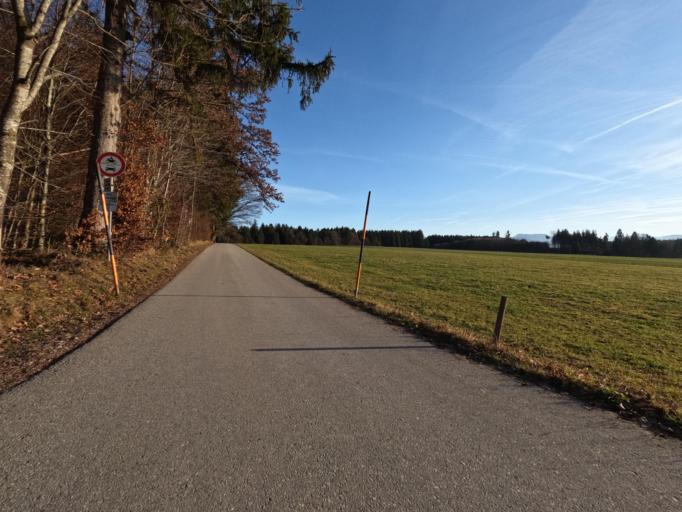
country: DE
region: Bavaria
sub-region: Upper Bavaria
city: Traunstein
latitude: 47.8999
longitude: 12.6357
